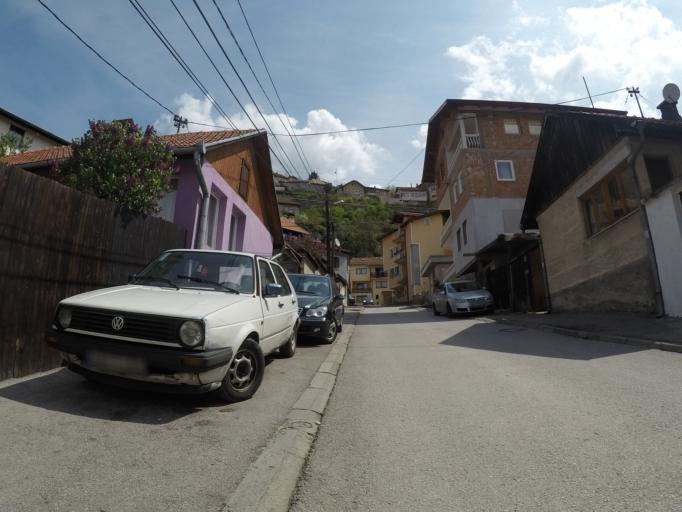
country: BA
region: Federation of Bosnia and Herzegovina
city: Kobilja Glava
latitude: 43.8556
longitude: 18.4361
